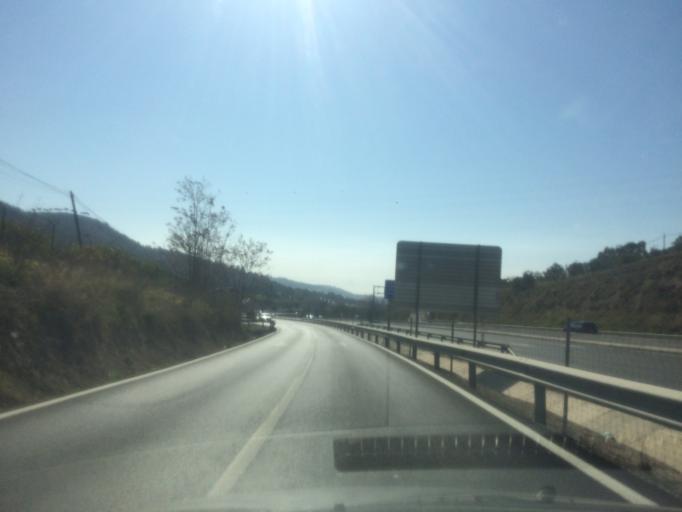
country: ES
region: Andalusia
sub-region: Provincia de Malaga
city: Malaga
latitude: 36.7706
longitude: -4.4253
